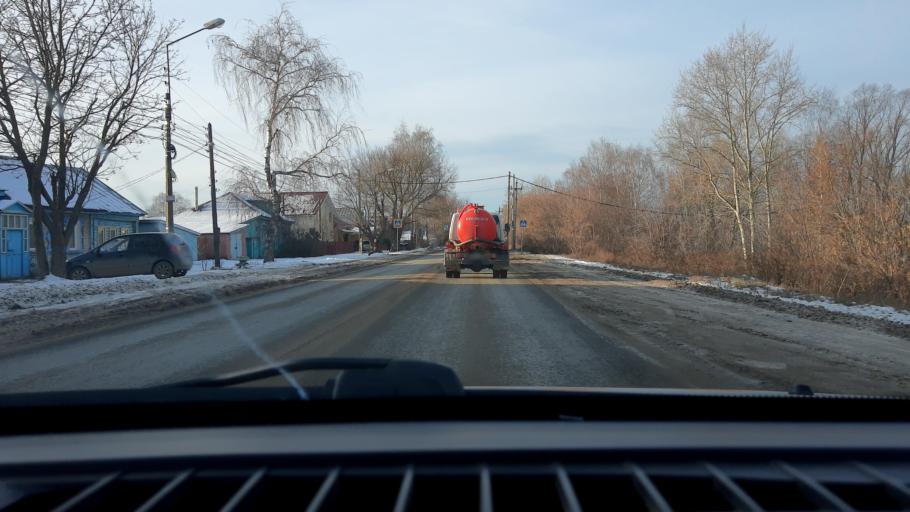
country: RU
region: Nizjnij Novgorod
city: Bor
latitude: 56.3654
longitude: 44.0793
